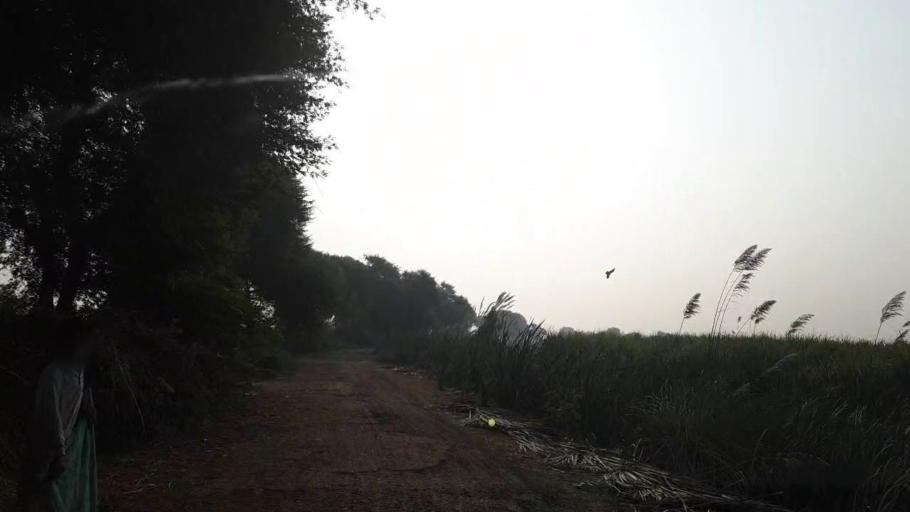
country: PK
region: Sindh
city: Tando Muhammad Khan
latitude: 25.1252
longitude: 68.5603
